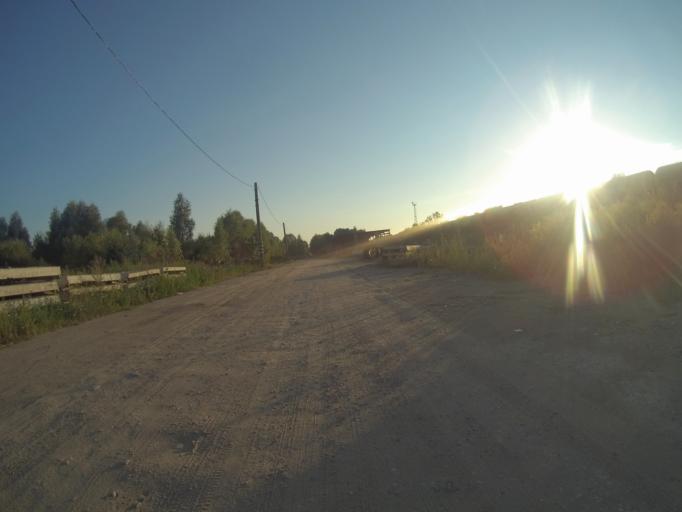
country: RU
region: Vladimir
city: Kommunar
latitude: 56.1367
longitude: 40.4509
